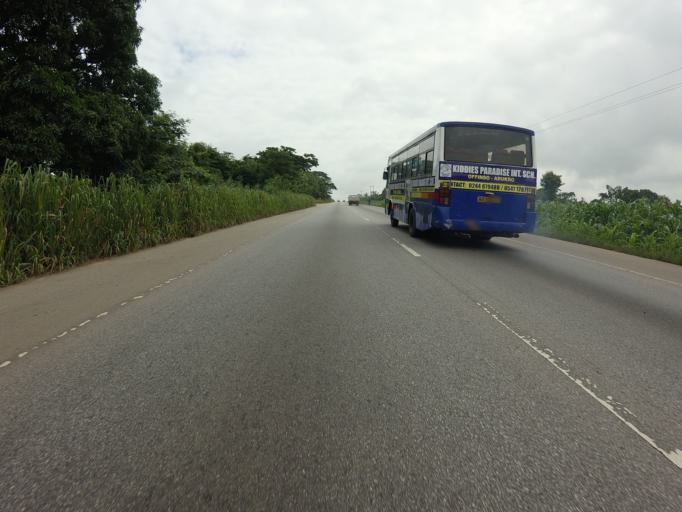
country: GH
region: Ashanti
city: Tafo
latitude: 6.9766
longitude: -1.6863
